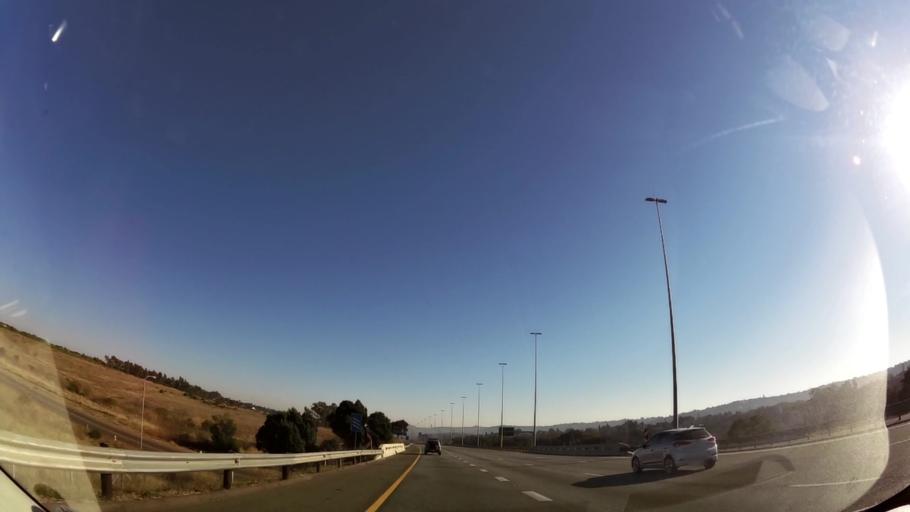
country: ZA
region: Gauteng
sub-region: City of Tshwane Metropolitan Municipality
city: Centurion
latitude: -25.8199
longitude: 28.2383
